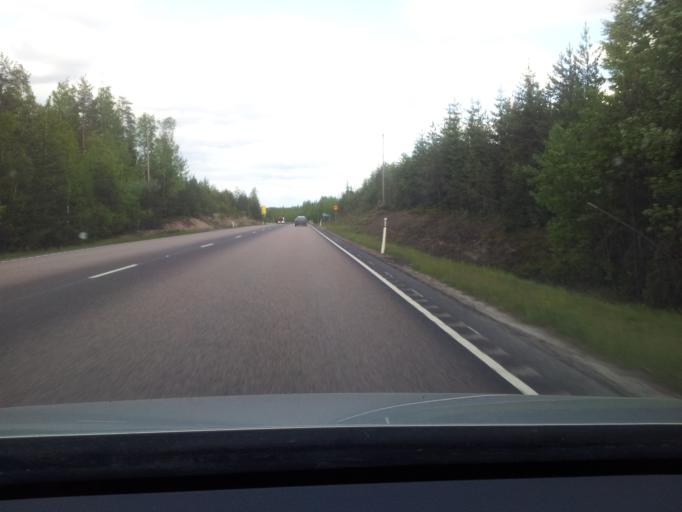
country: FI
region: South Karelia
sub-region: Lappeenranta
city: Taavetti
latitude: 60.9170
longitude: 27.4316
